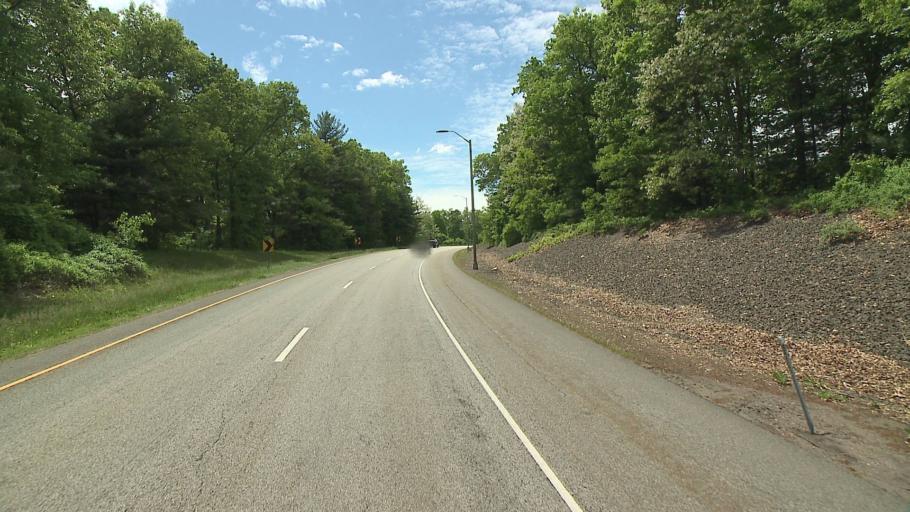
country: US
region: Connecticut
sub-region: Hartford County
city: Windsor Locks
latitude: 41.9010
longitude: -72.6385
